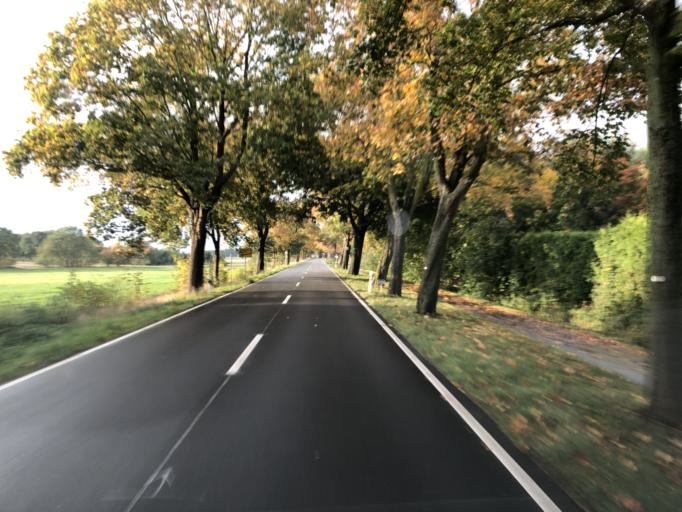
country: DE
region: Lower Saxony
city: Neu Wulmstorf
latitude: 53.4451
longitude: 9.8028
